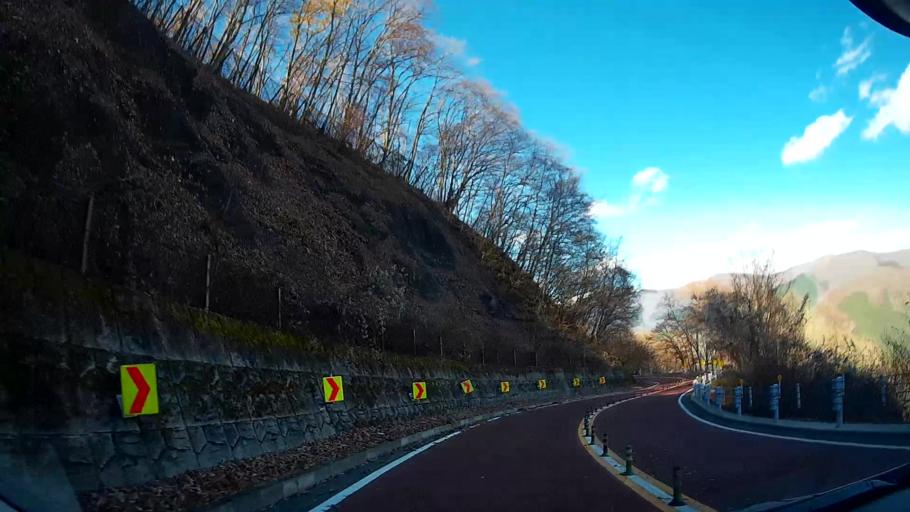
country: JP
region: Yamanashi
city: Uenohara
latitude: 35.7657
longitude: 139.0352
